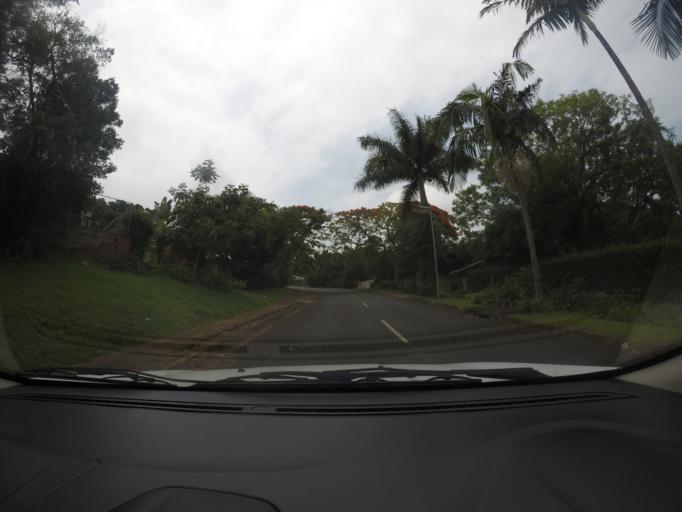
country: ZA
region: KwaZulu-Natal
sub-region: uThungulu District Municipality
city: Empangeni
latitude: -28.7519
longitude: 31.8922
